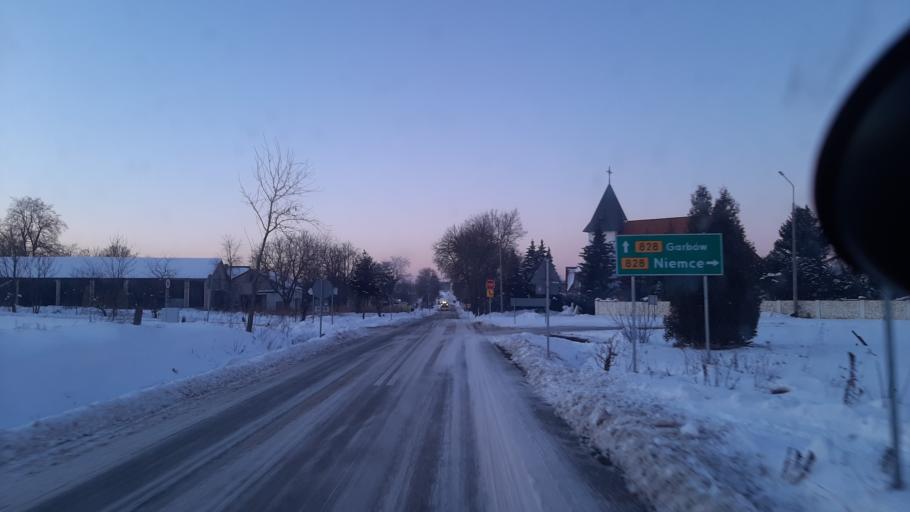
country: PL
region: Lublin Voivodeship
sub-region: Powiat lubelski
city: Niemce
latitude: 51.3596
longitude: 22.5321
